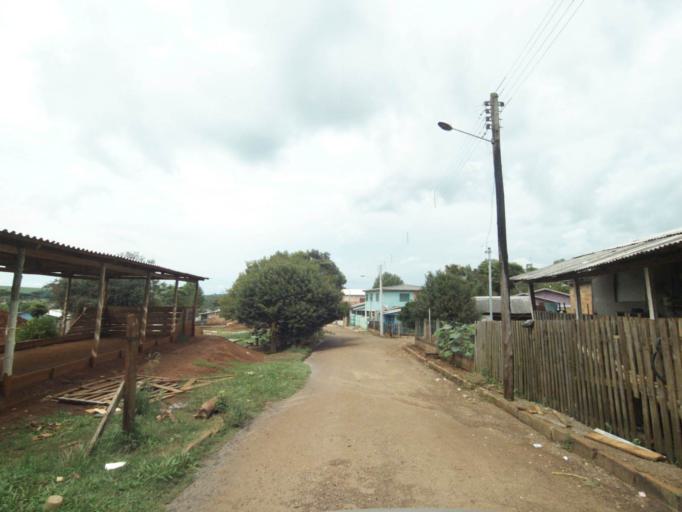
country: BR
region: Rio Grande do Sul
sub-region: Lagoa Vermelha
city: Lagoa Vermelha
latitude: -28.2263
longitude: -51.5137
